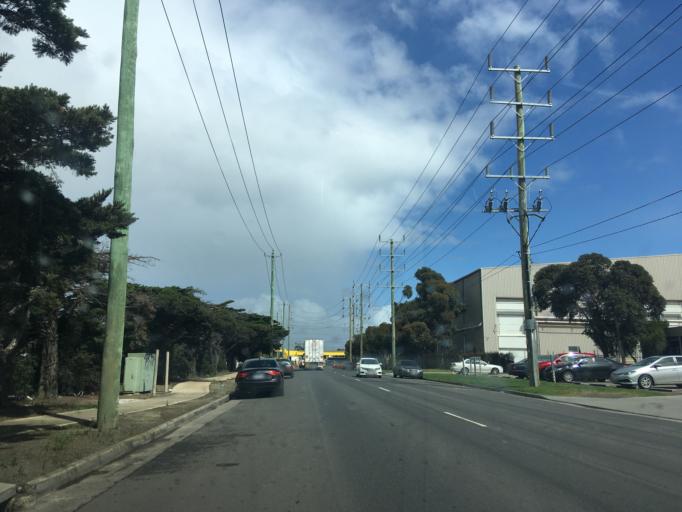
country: AU
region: Victoria
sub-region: Brimbank
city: Sunshine West
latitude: -37.8272
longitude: 144.7966
